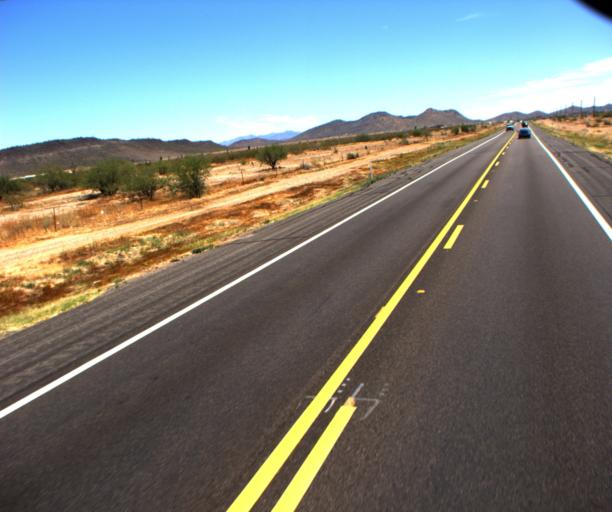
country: US
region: Arizona
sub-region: Maricopa County
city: Anthem
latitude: 33.7982
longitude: -112.1636
